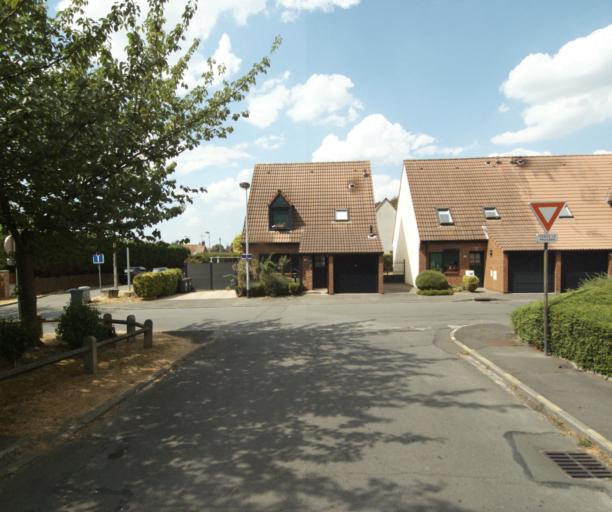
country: FR
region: Nord-Pas-de-Calais
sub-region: Departement du Nord
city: Neuville-en-Ferrain
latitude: 50.7431
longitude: 3.1691
